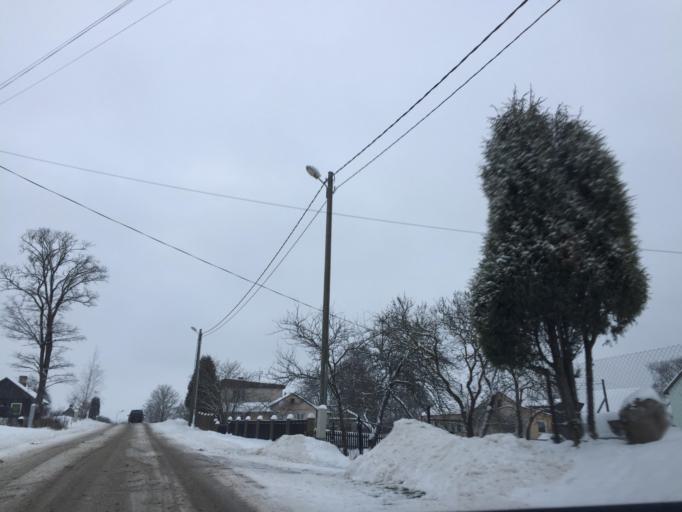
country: LV
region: Smiltene
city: Smiltene
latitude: 57.4161
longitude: 25.8938
